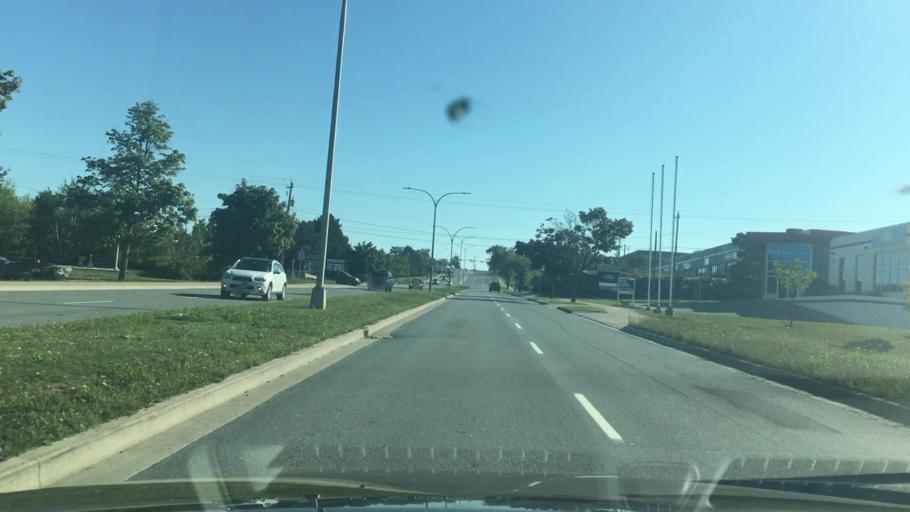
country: CA
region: Nova Scotia
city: Dartmouth
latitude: 44.7099
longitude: -63.6047
